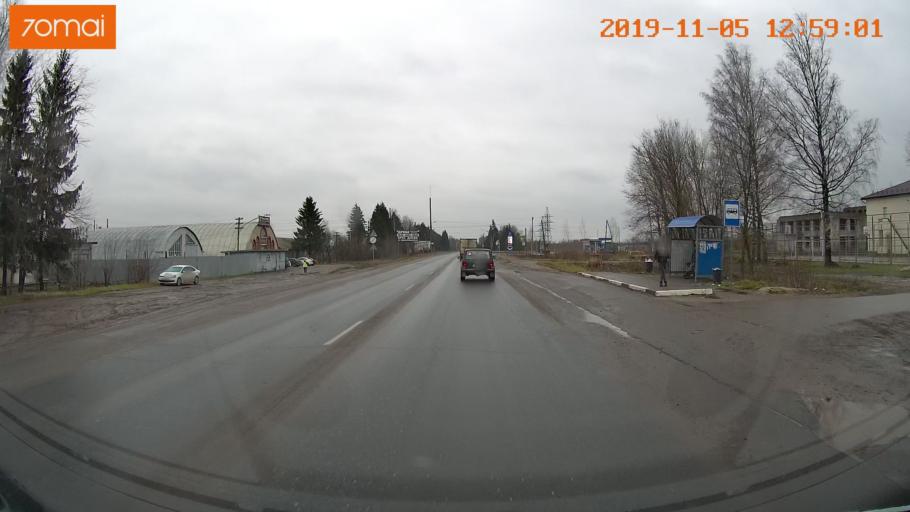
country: RU
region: Ivanovo
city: Kokhma
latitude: 56.9200
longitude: 41.1238
